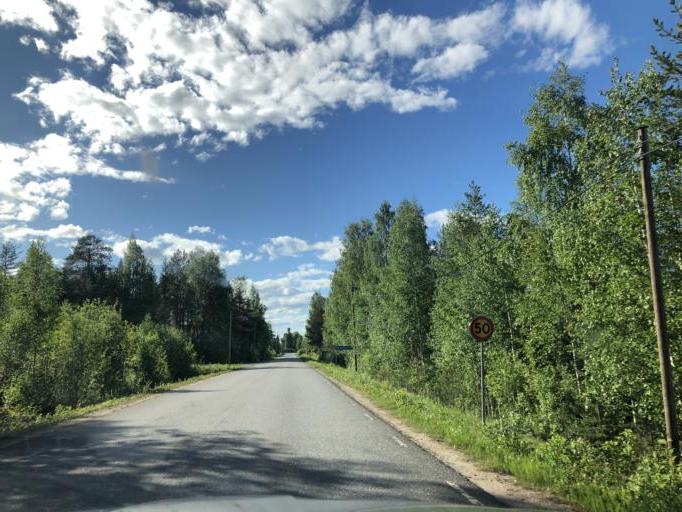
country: SE
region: Norrbotten
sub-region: Overkalix Kommun
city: OEverkalix
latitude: 66.3188
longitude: 22.8678
